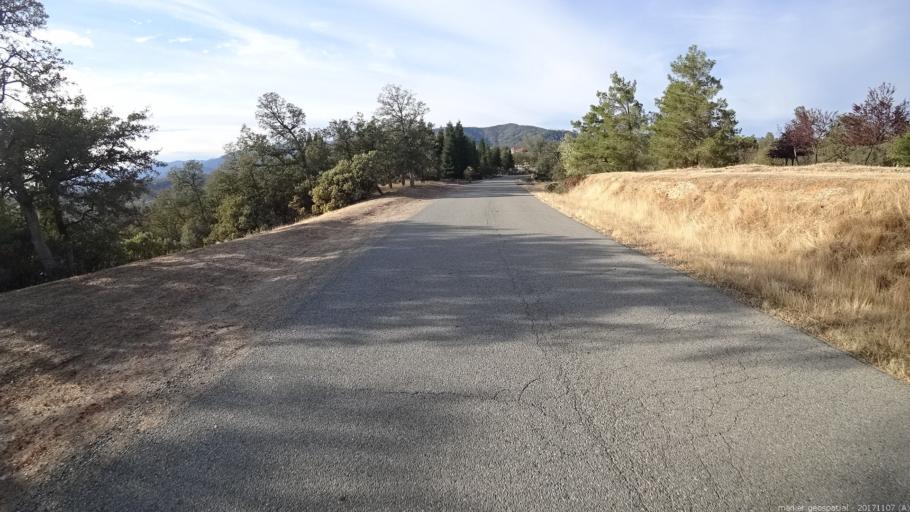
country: US
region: California
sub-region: Shasta County
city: Shasta
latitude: 40.5074
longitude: -122.4725
